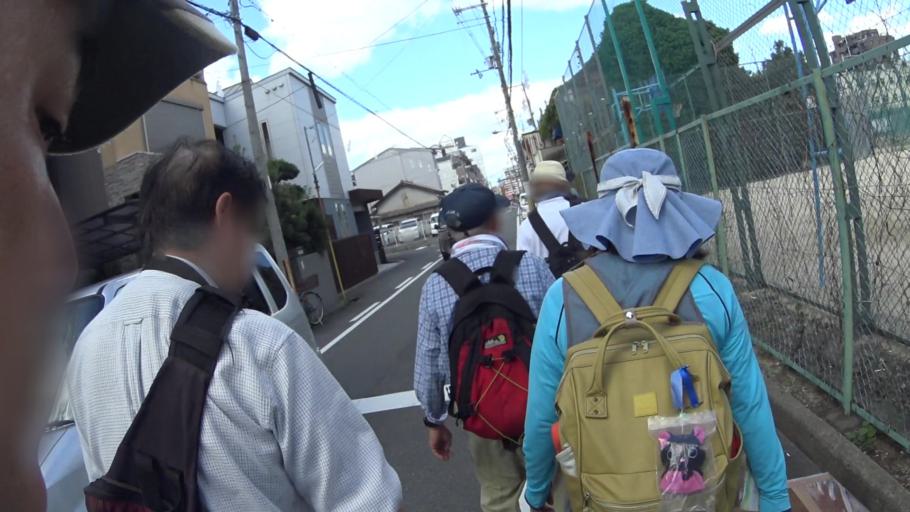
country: JP
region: Osaka
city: Yao
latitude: 34.6463
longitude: 135.5523
